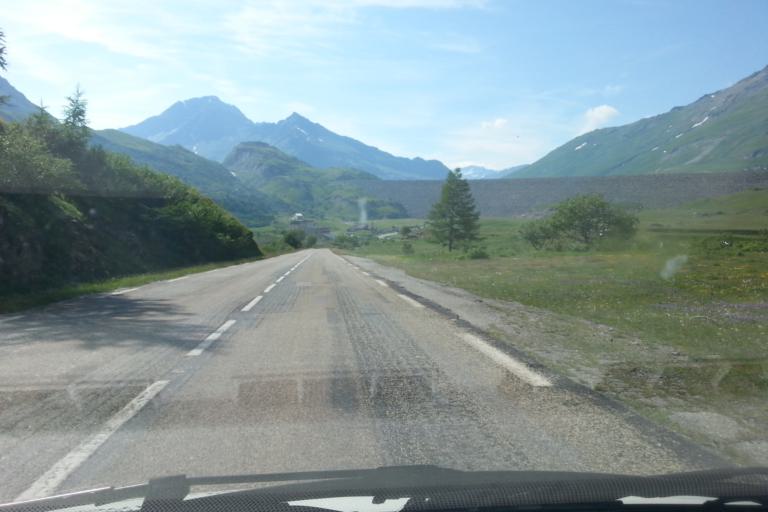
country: IT
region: Piedmont
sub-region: Provincia di Torino
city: Moncenisio
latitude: 45.2149
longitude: 6.9639
